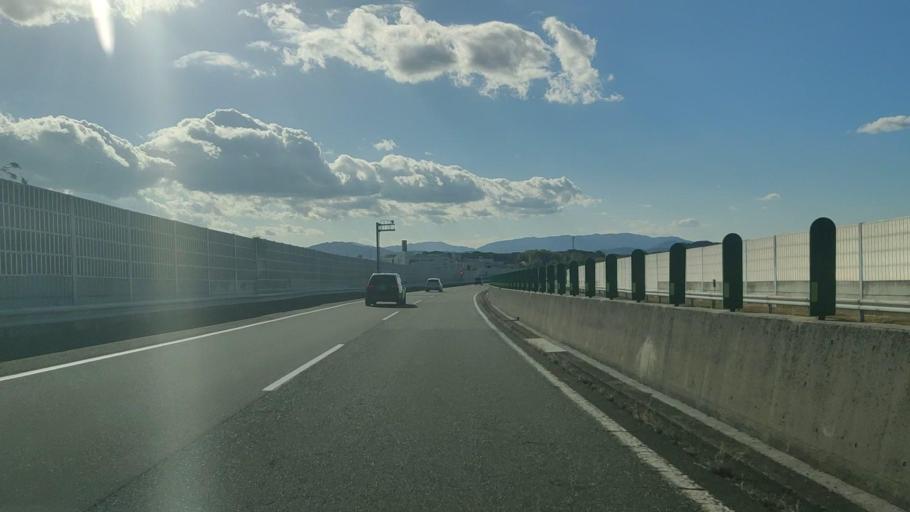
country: JP
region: Fukuoka
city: Nakama
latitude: 33.8221
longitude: 130.7601
